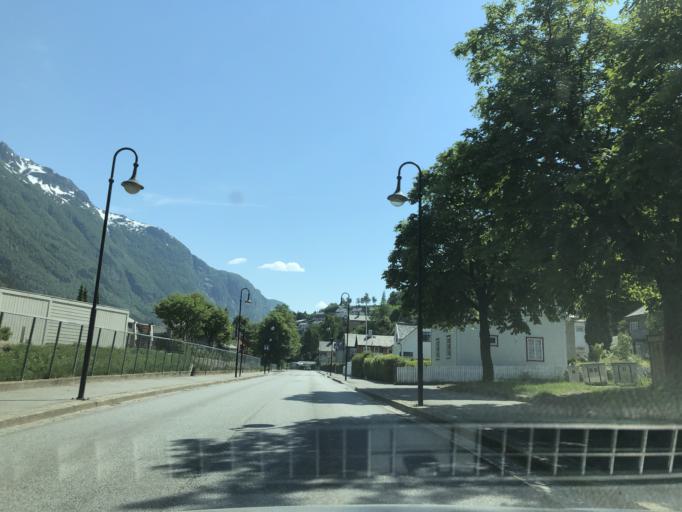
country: NO
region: Hordaland
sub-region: Odda
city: Odda
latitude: 60.0690
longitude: 6.5414
